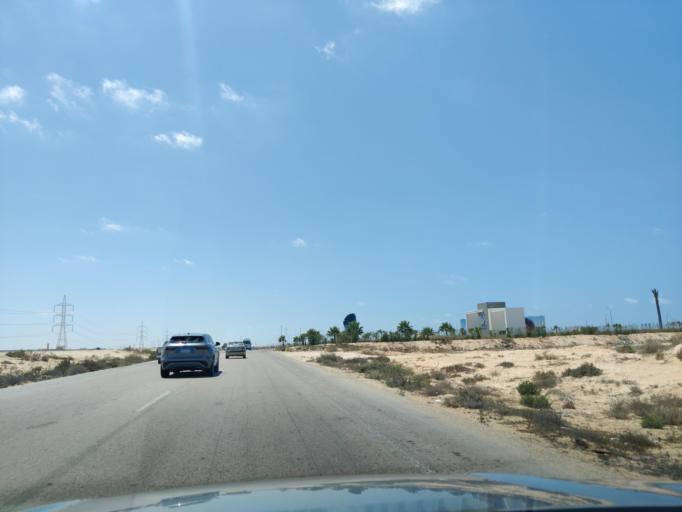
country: EG
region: Muhafazat Matruh
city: Al `Alamayn
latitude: 31.0682
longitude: 28.1700
